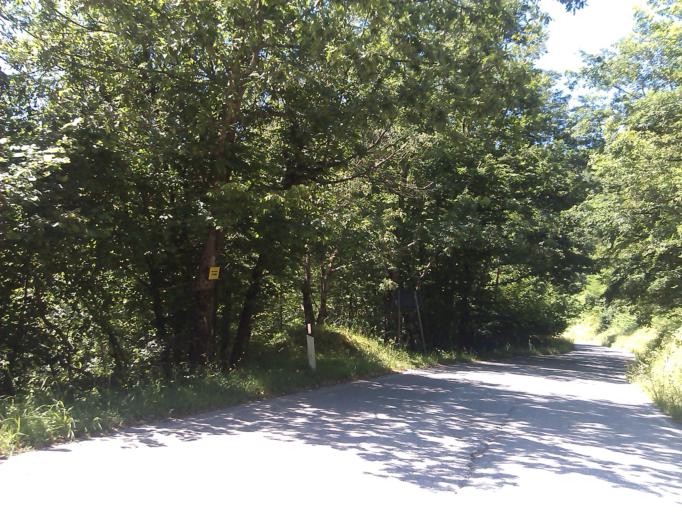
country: IT
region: Tuscany
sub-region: Provincia di Pistoia
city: Sambuca Pistoiese
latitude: 44.0762
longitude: 11.0526
